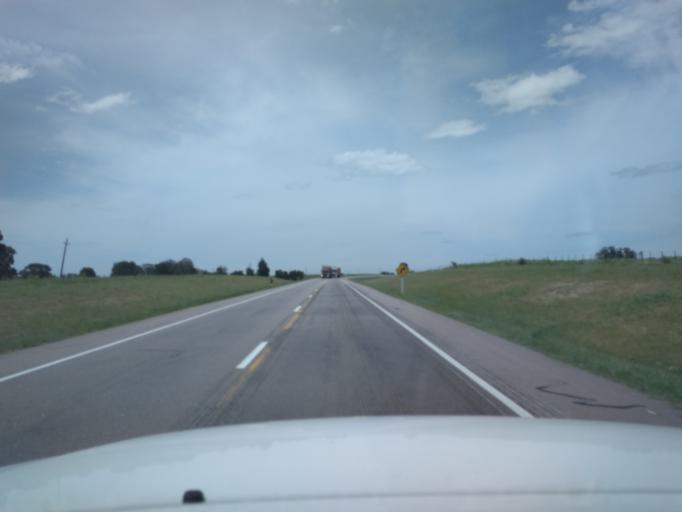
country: UY
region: Florida
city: Cardal
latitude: -34.3203
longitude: -56.2428
